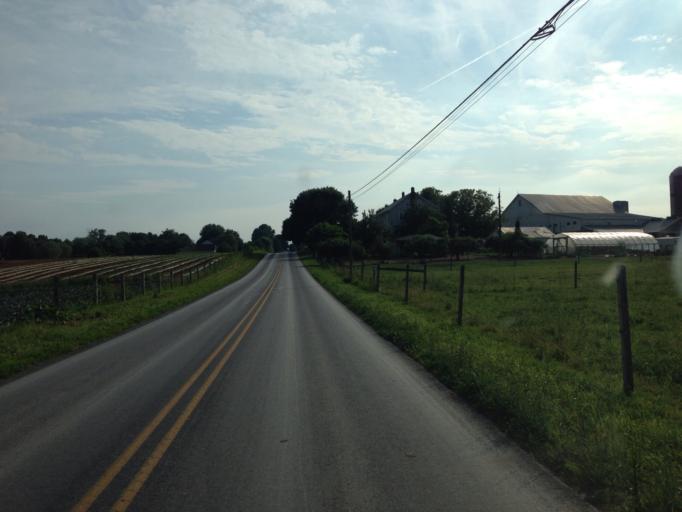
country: US
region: Pennsylvania
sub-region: Lancaster County
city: Brownstown
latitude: 40.0553
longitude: -76.1967
